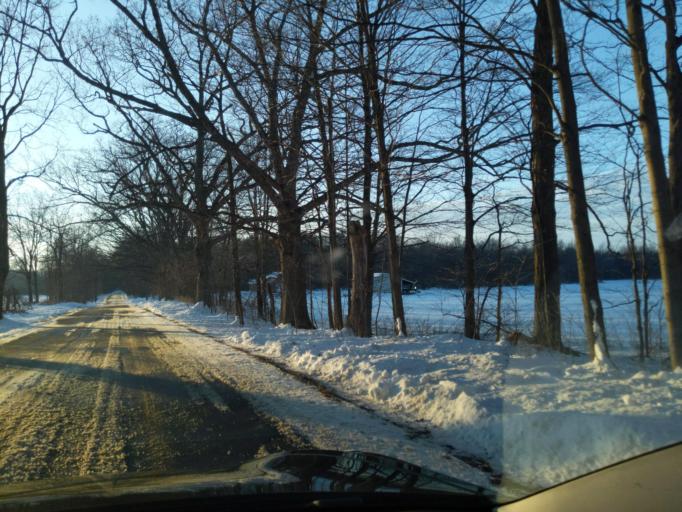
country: US
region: Michigan
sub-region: Ingham County
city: Webberville
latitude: 42.5683
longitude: -84.1465
